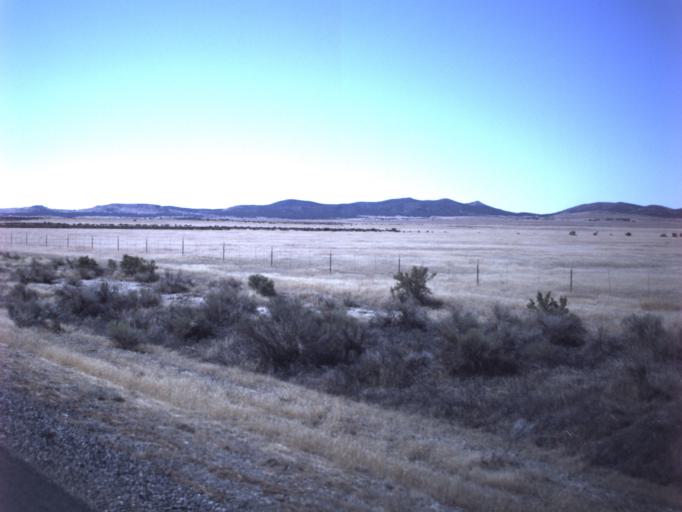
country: US
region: Utah
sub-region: Tooele County
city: Grantsville
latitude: 40.3012
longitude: -112.7429
